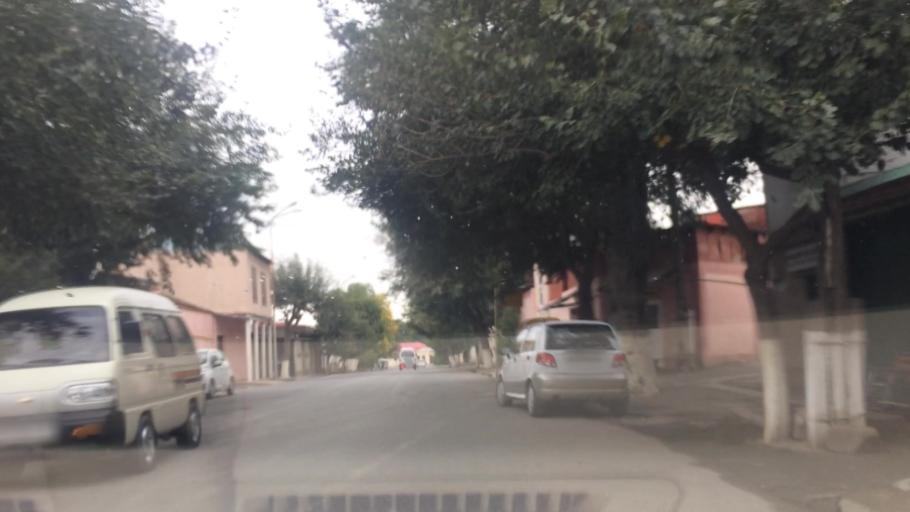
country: UZ
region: Samarqand
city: Samarqand
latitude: 39.6592
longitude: 66.9727
